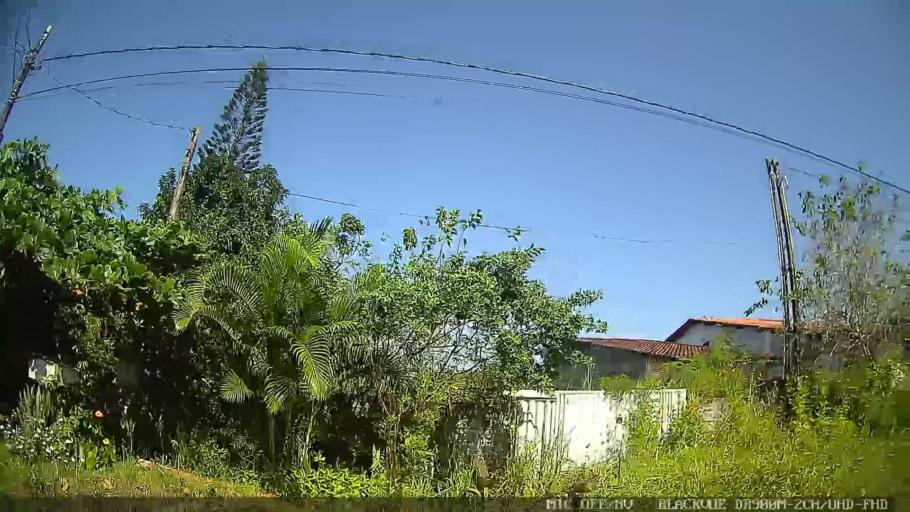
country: BR
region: Sao Paulo
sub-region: Itanhaem
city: Itanhaem
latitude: -24.2071
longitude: -46.8543
